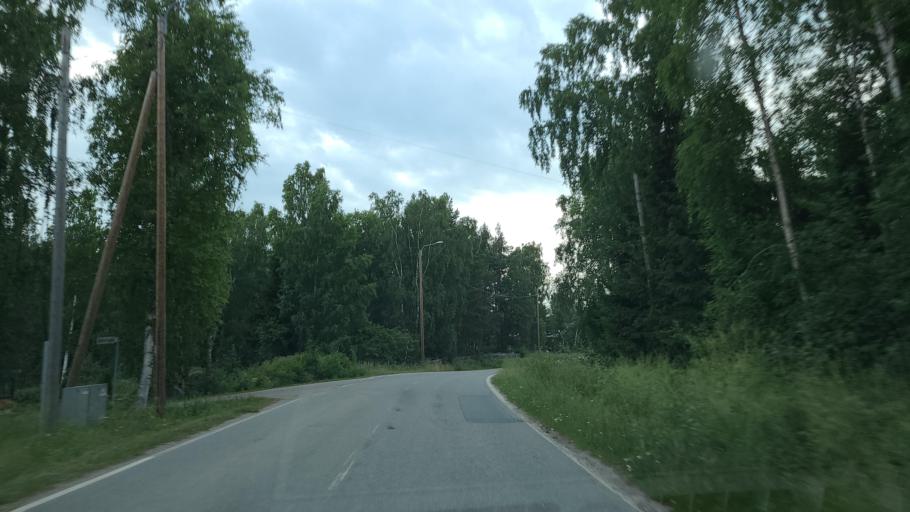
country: FI
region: Ostrobothnia
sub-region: Vaasa
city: Replot
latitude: 63.1780
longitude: 21.2775
